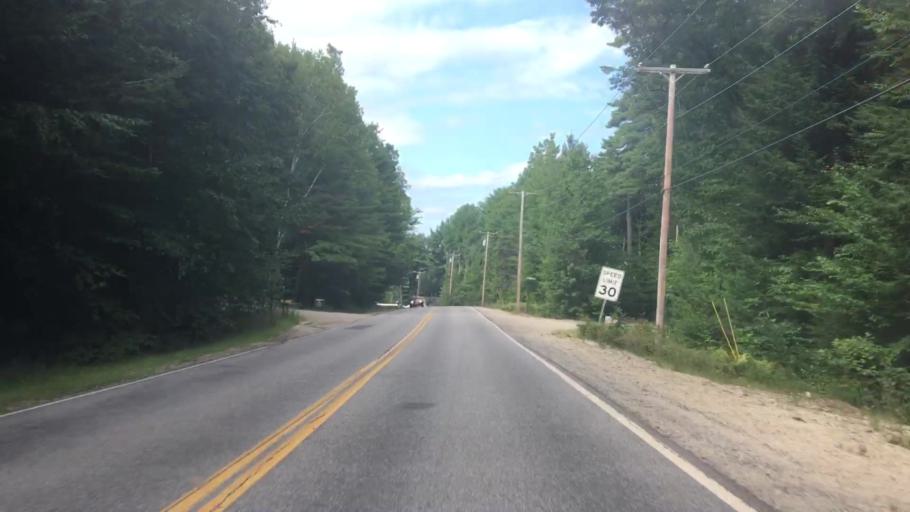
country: US
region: Maine
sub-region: Oxford County
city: Oxford
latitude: 44.0993
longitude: -70.5097
